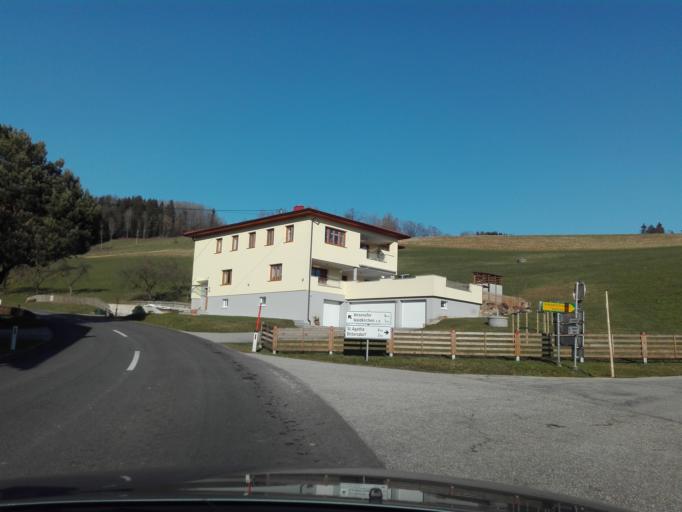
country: AT
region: Upper Austria
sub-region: Politischer Bezirk Rohrbach
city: Pfarrkirchen im Muehlkreis
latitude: 48.4008
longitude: 13.8159
